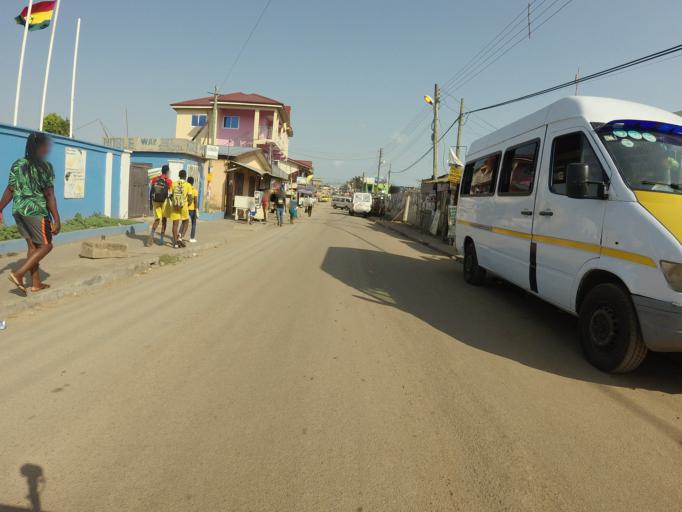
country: GH
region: Greater Accra
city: Dome
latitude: 5.6098
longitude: -0.2480
